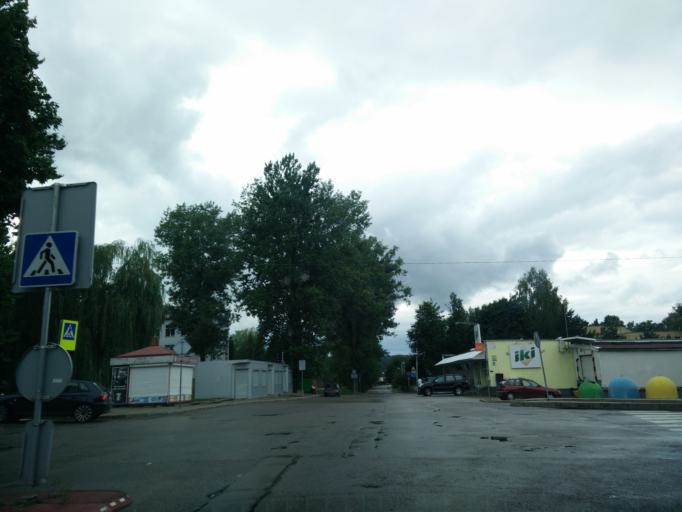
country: LT
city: Grigiskes
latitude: 54.6709
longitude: 25.0916
